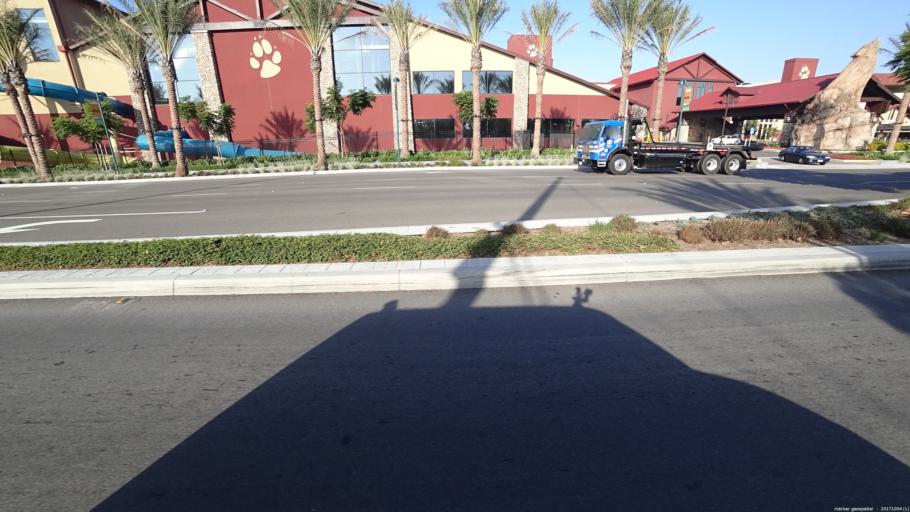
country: US
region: California
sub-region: Orange County
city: Garden Grove
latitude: 33.7788
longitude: -117.9148
